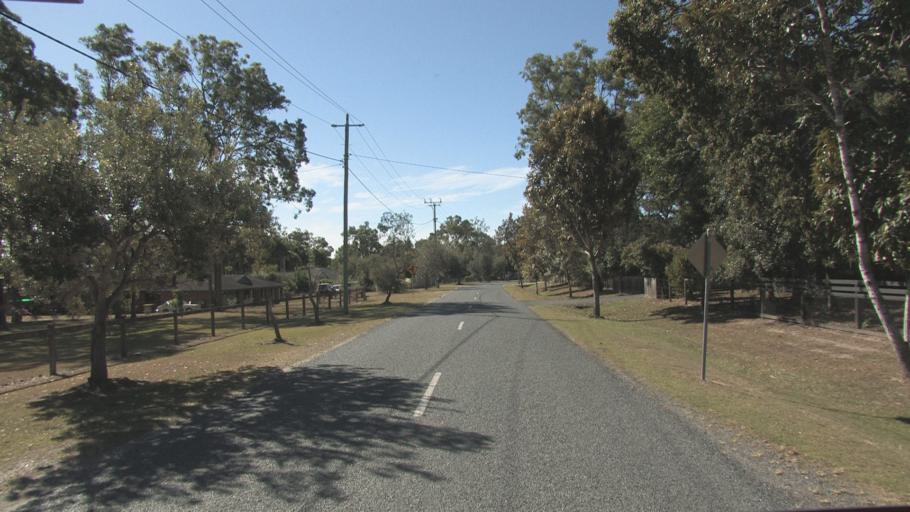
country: AU
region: Queensland
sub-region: Logan
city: North Maclean
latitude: -27.7432
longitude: 152.9552
